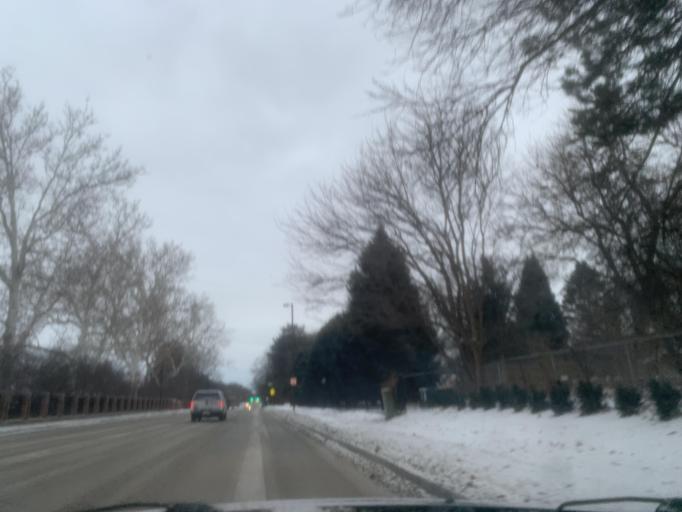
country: US
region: Nebraska
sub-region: Douglas County
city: Ralston
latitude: 41.2583
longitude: -96.0526
